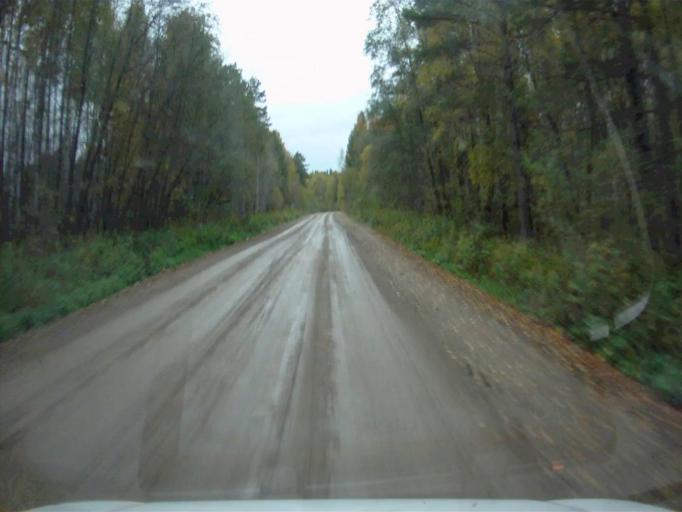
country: RU
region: Chelyabinsk
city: Nyazepetrovsk
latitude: 56.1019
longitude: 59.3877
